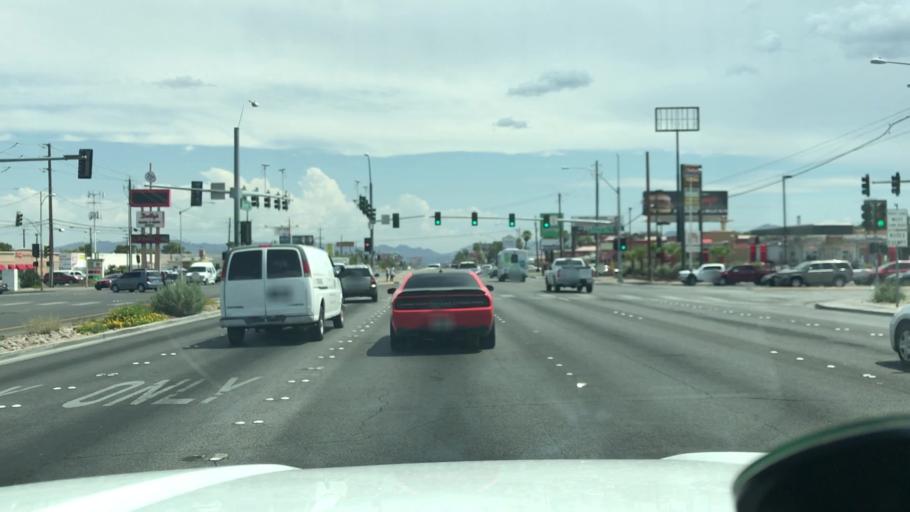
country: US
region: Nevada
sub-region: Clark County
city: Winchester
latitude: 36.1305
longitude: -115.0844
